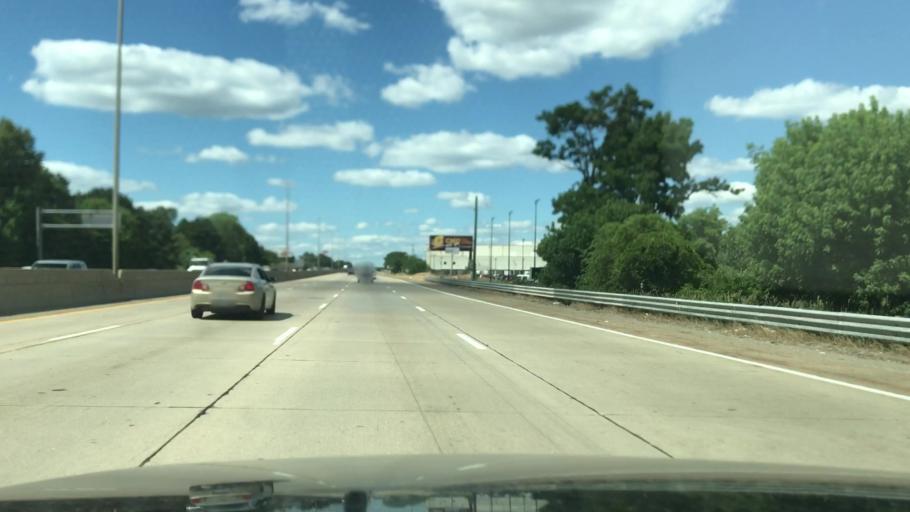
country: US
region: Michigan
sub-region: Kent County
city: Cutlerville
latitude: 42.8697
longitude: -85.6803
